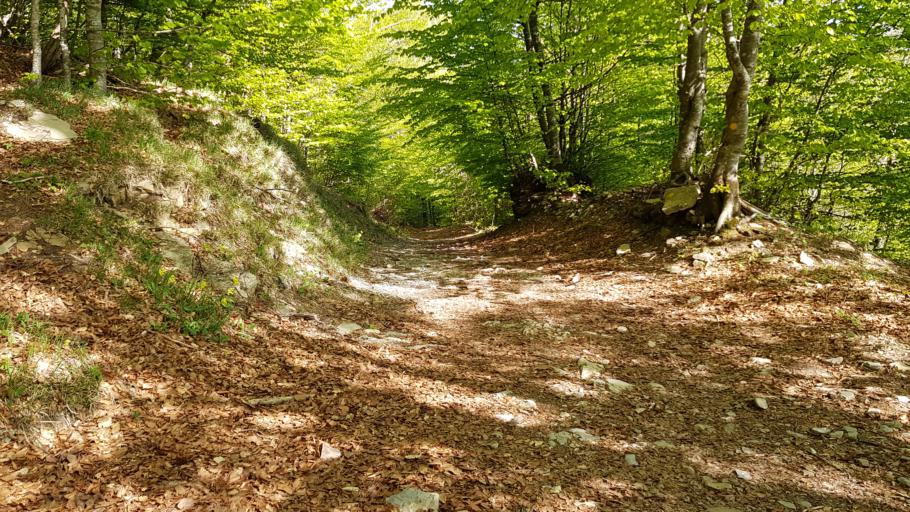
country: IT
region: Liguria
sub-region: Provincia di Genova
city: Fascia
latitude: 44.6060
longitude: 9.2038
